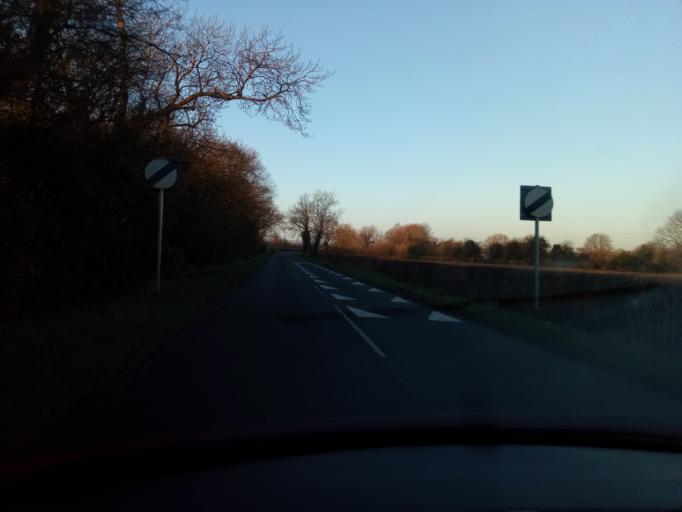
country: GB
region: England
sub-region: Leicestershire
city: Barrow upon Soar
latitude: 52.7733
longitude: -1.1297
